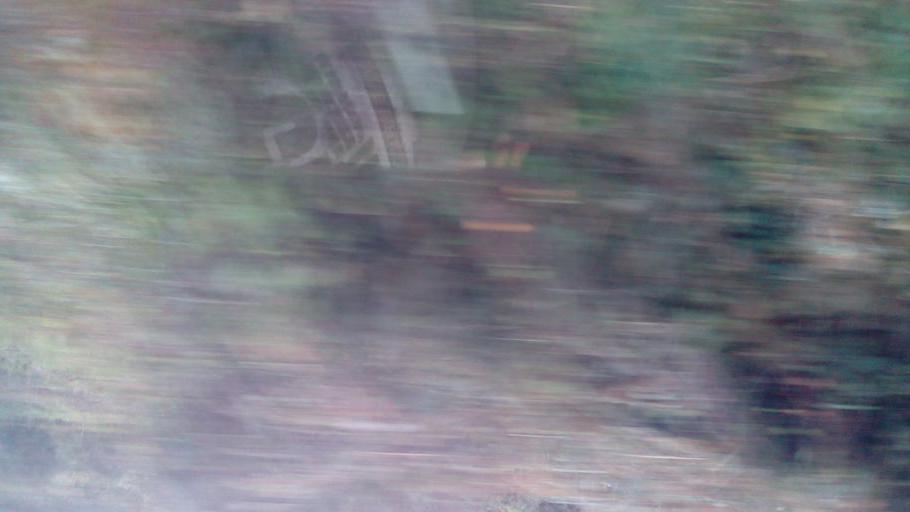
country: TW
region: Taiwan
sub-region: Hualien
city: Hualian
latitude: 24.3472
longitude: 121.3158
